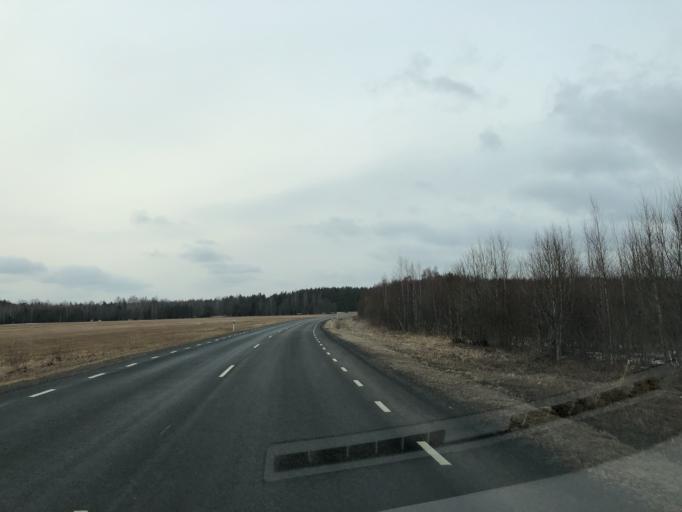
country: EE
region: Viljandimaa
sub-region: Suure-Jaani vald
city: Suure-Jaani
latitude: 58.5669
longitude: 25.3990
